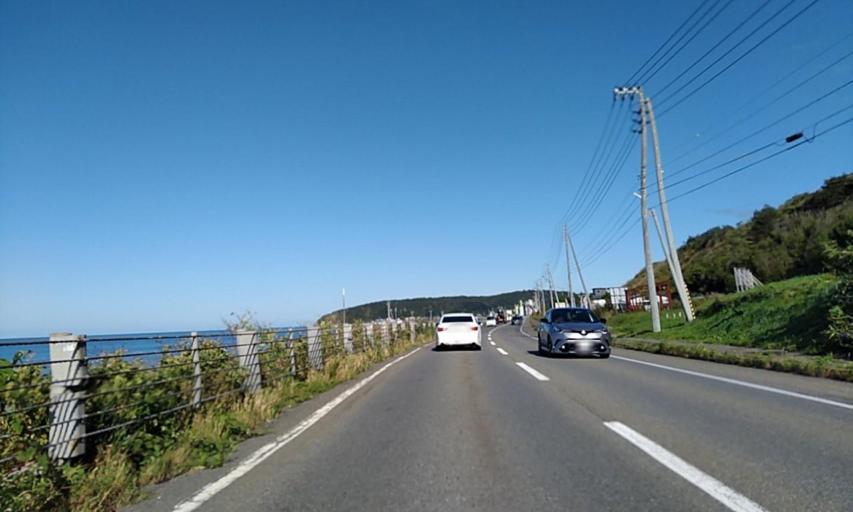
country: JP
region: Hokkaido
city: Shizunai-furukawacho
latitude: 42.3517
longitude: 142.3247
